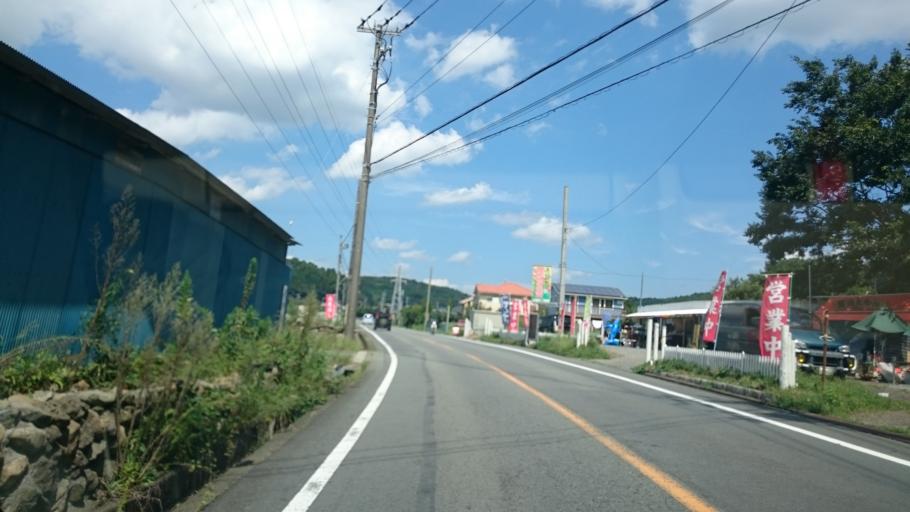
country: JP
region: Shizuoka
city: Mishima
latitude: 35.1908
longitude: 138.9222
